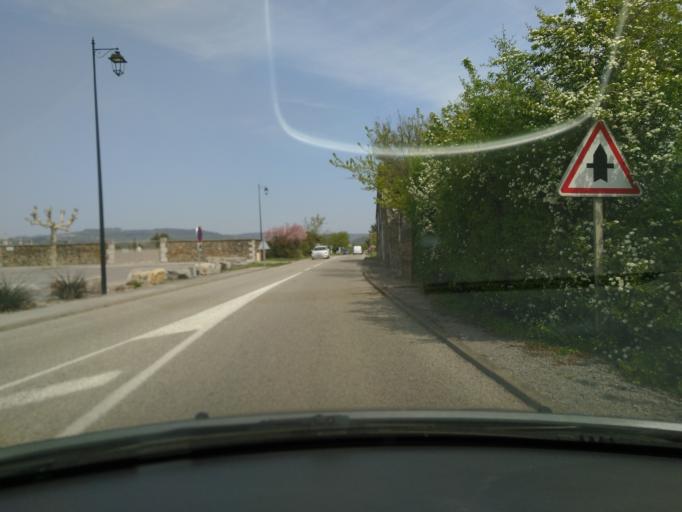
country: FR
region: Rhone-Alpes
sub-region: Departement de l'Ardeche
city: Lavilledieu
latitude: 44.5556
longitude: 4.4520
